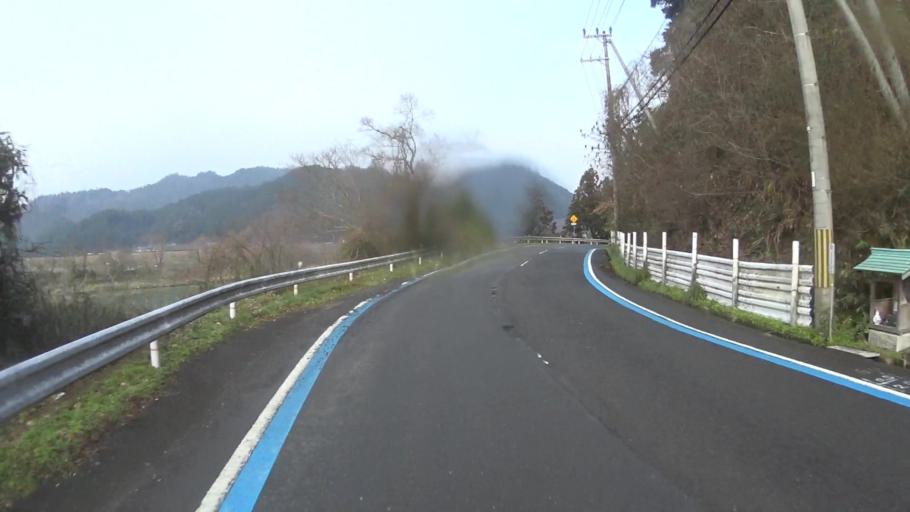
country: JP
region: Kyoto
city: Maizuru
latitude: 35.4354
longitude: 135.2599
